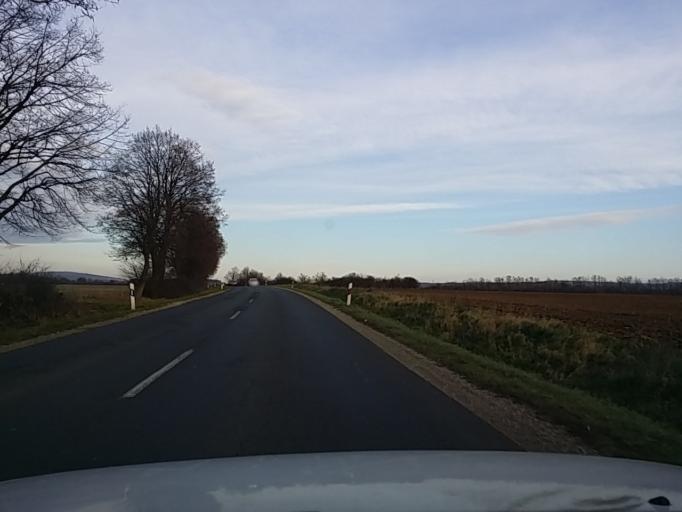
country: HU
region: Veszprem
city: Urkut
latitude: 46.9903
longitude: 17.7205
